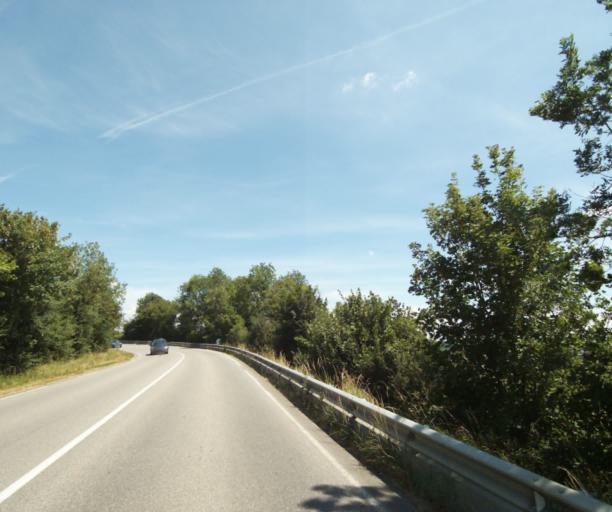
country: FR
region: Lorraine
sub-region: Departement de Meurthe-et-Moselle
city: Luneville
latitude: 48.6099
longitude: 6.4913
